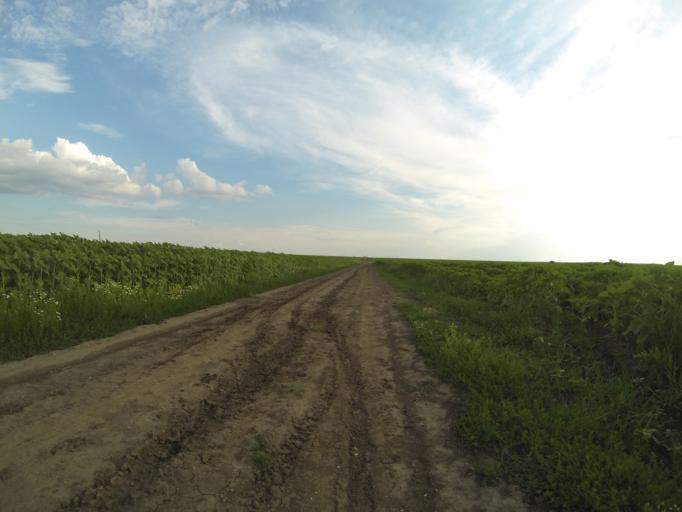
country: RO
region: Dolj
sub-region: Comuna Caloparu
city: Salcuta
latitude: 44.1417
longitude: 23.6930
